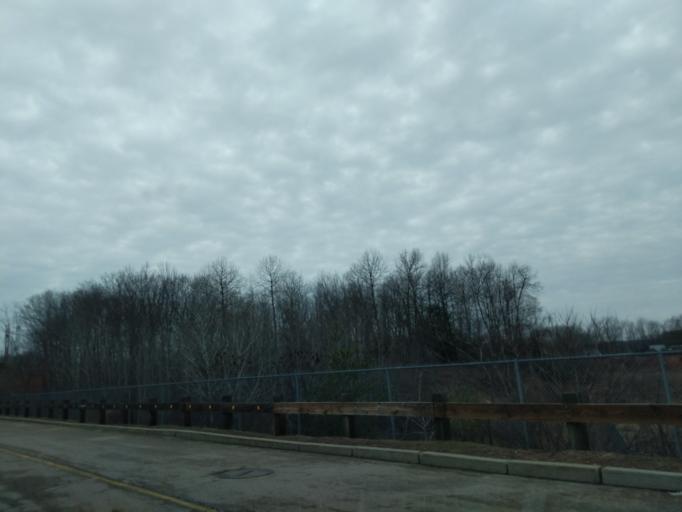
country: US
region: Massachusetts
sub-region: Worcester County
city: Whitinsville
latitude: 42.1084
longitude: -71.6991
